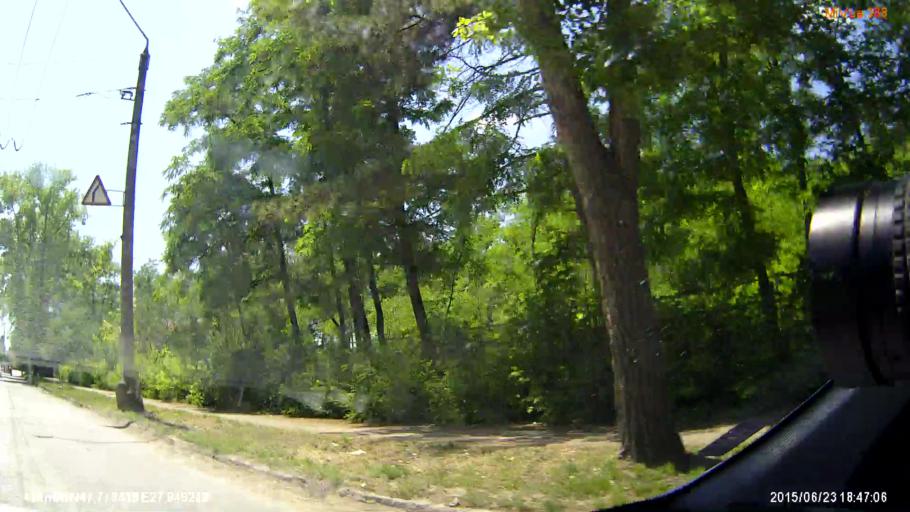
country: MD
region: Balti
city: Balti
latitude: 47.7736
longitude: 27.9494
